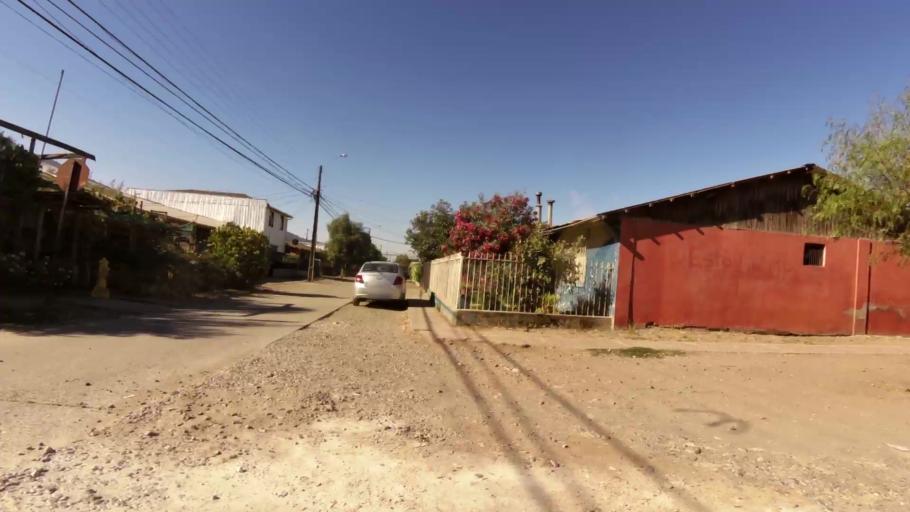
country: CL
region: O'Higgins
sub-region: Provincia de Colchagua
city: Chimbarongo
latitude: -34.5743
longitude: -70.9960
